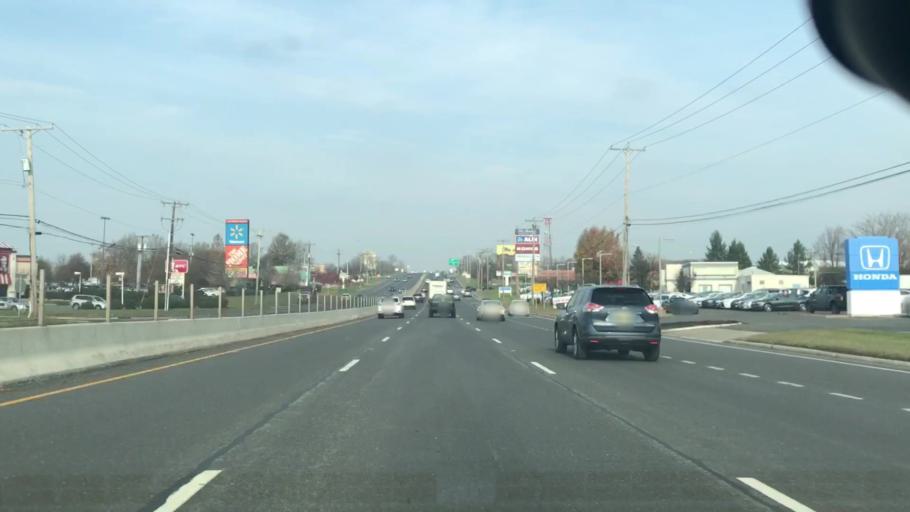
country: US
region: New Jersey
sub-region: Middlesex County
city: Madison Park
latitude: 40.4485
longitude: -74.2991
